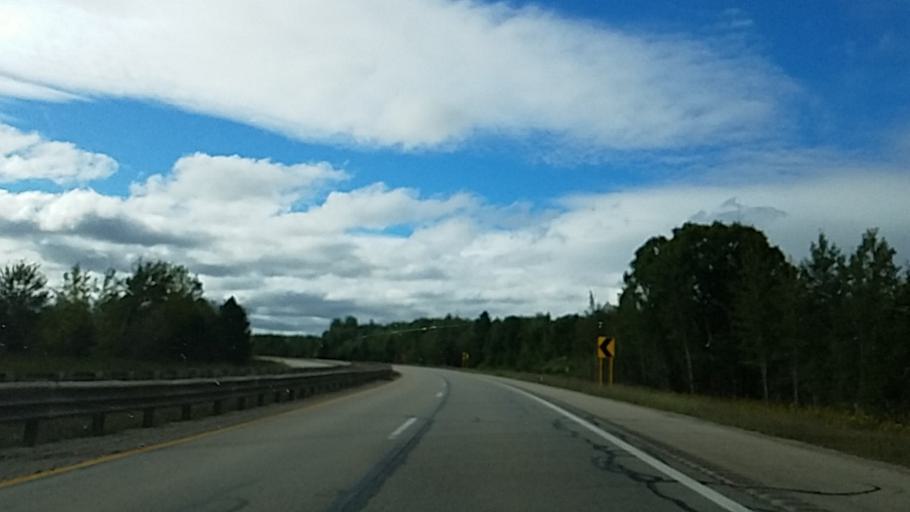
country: US
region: Michigan
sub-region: Mackinac County
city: Saint Ignace
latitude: 45.7671
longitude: -84.7352
